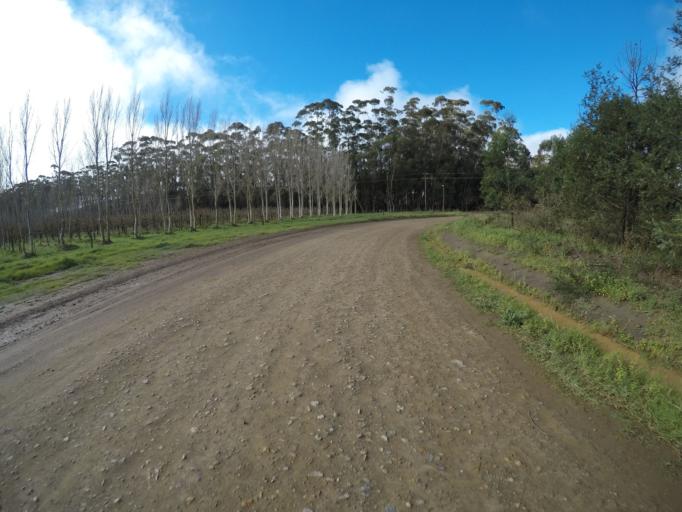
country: ZA
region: Western Cape
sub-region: Cape Winelands District Municipality
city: Ashton
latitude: -34.1113
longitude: 19.7970
